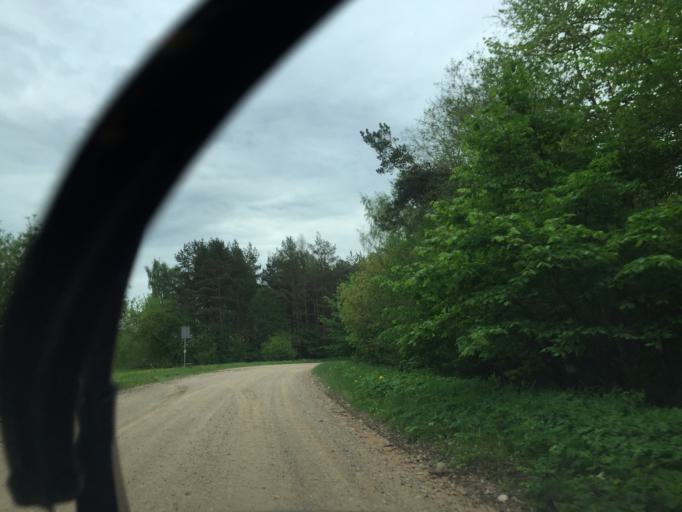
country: LV
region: Lielvarde
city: Lielvarde
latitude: 56.8077
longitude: 24.8281
